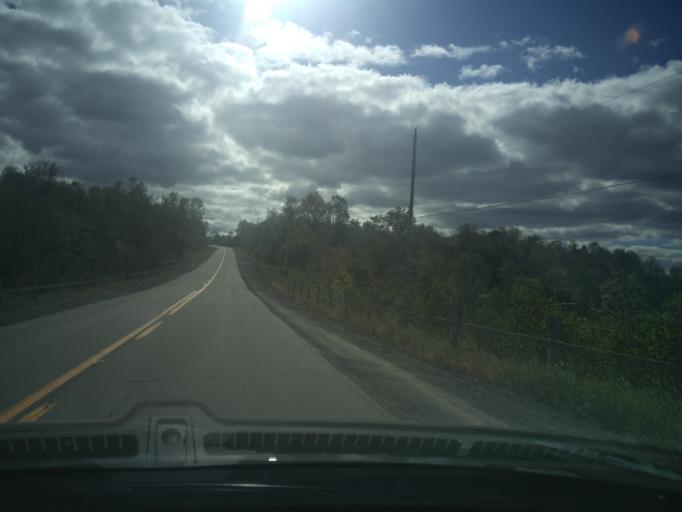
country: CA
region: Ontario
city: Perth
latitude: 44.7560
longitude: -76.3884
